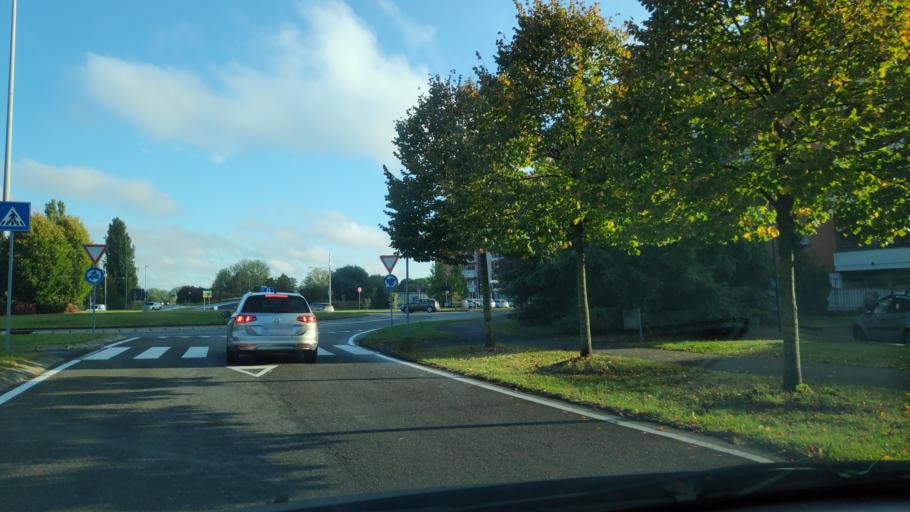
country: IT
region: Lombardy
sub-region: Citta metropolitana di Milano
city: Opera
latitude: 45.3821
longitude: 9.2132
